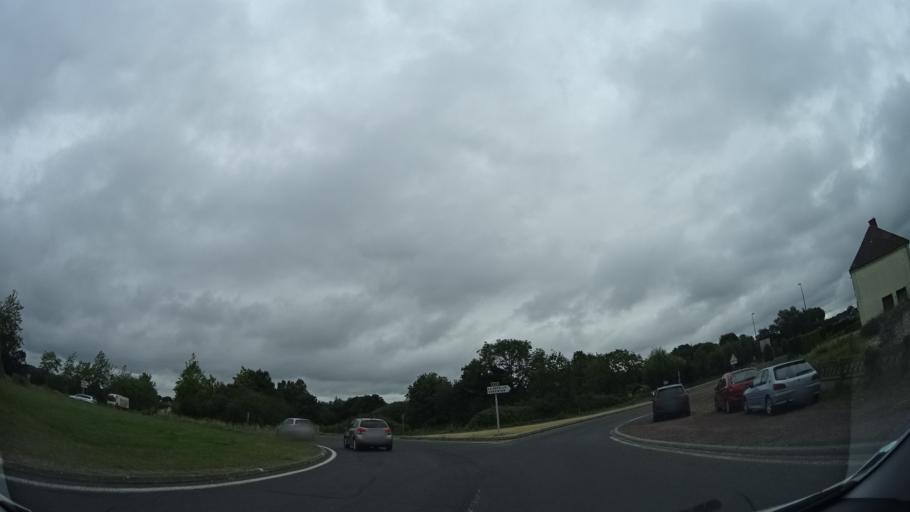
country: FR
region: Lower Normandy
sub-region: Departement de la Manche
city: La Haye-du-Puits
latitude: 49.2947
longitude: -1.5579
